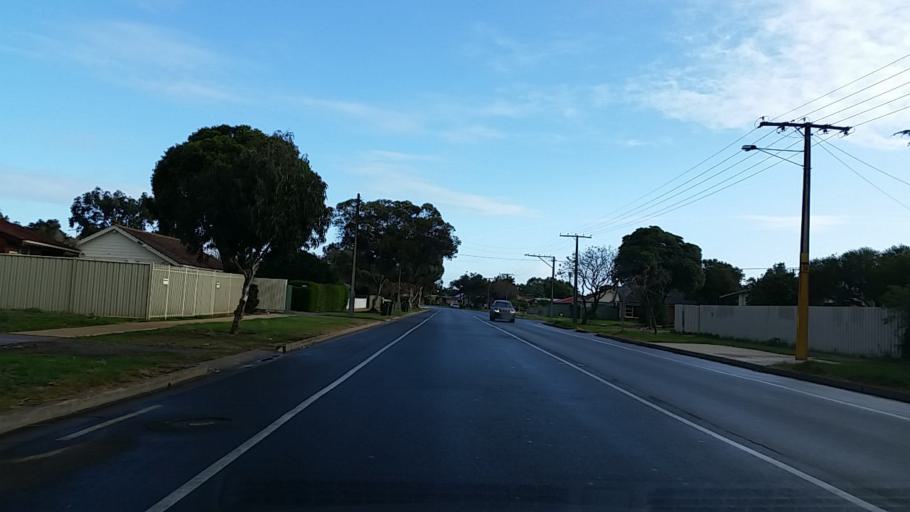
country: AU
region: South Australia
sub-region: Playford
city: Smithfield
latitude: -34.6898
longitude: 138.6743
